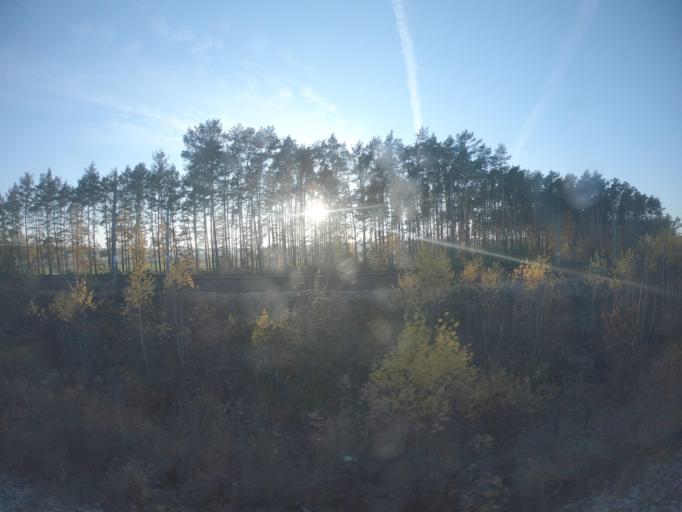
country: PL
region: Lubusz
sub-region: Powiat slubicki
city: Rzepin
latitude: 52.3274
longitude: 14.8427
